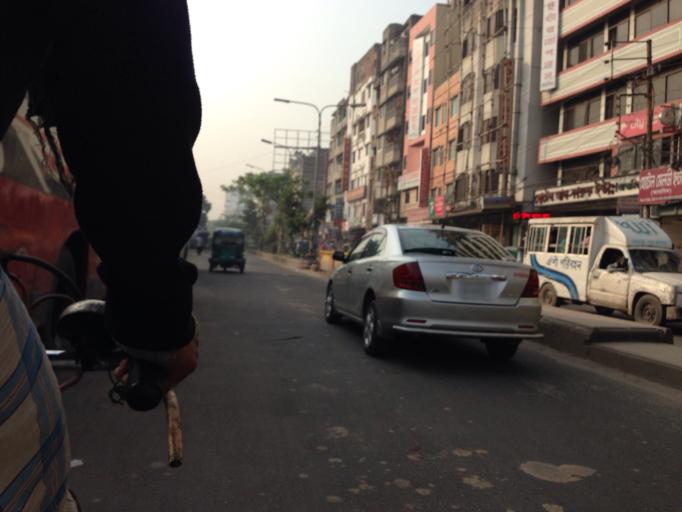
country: BD
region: Dhaka
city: Paltan
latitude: 23.7314
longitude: 90.4253
